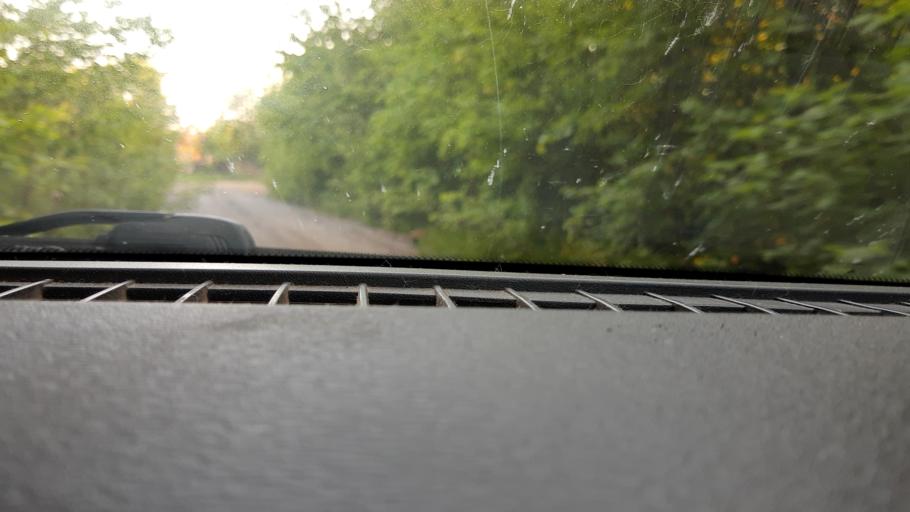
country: RU
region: Bashkortostan
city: Iglino
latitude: 54.7709
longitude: 56.2115
